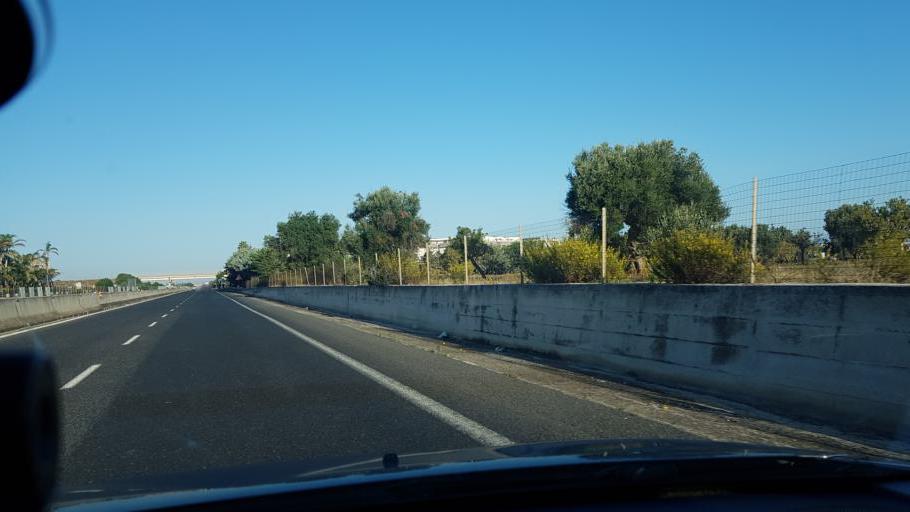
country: IT
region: Apulia
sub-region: Provincia di Bari
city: Monopoli
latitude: 40.9286
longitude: 17.3059
